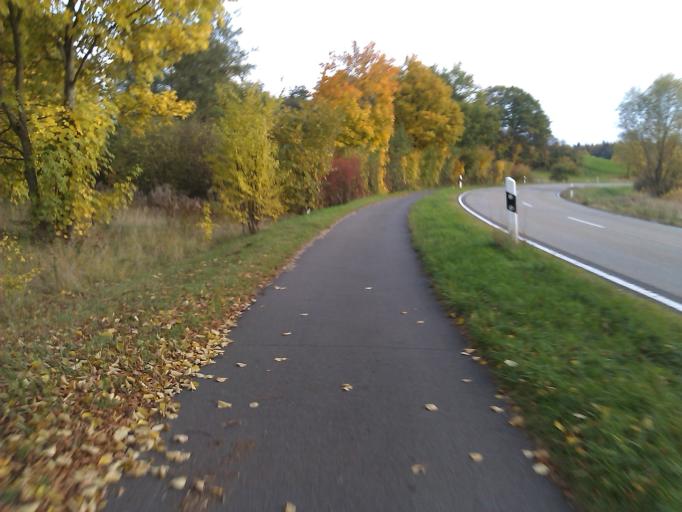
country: DE
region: Rheinland-Pfalz
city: Schneckenhausen
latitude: 49.5326
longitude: 7.7479
